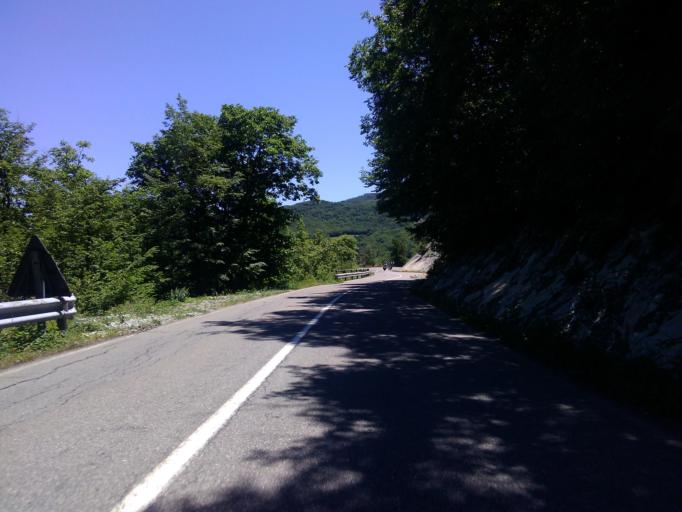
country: IT
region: Emilia-Romagna
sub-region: Provincia di Parma
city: Terenzo
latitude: 44.5793
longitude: 10.0656
